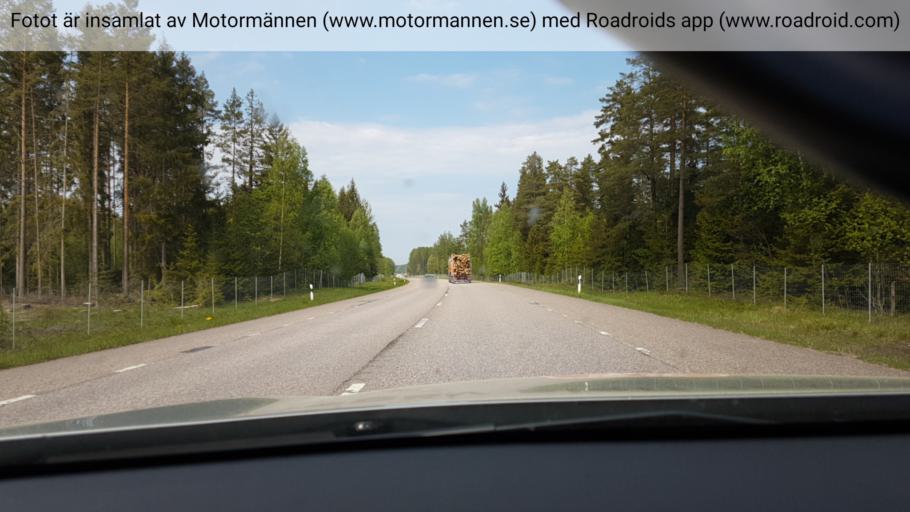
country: SE
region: Uppsala
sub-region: Alvkarleby Kommun
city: AElvkarleby
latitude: 60.5672
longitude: 17.4671
